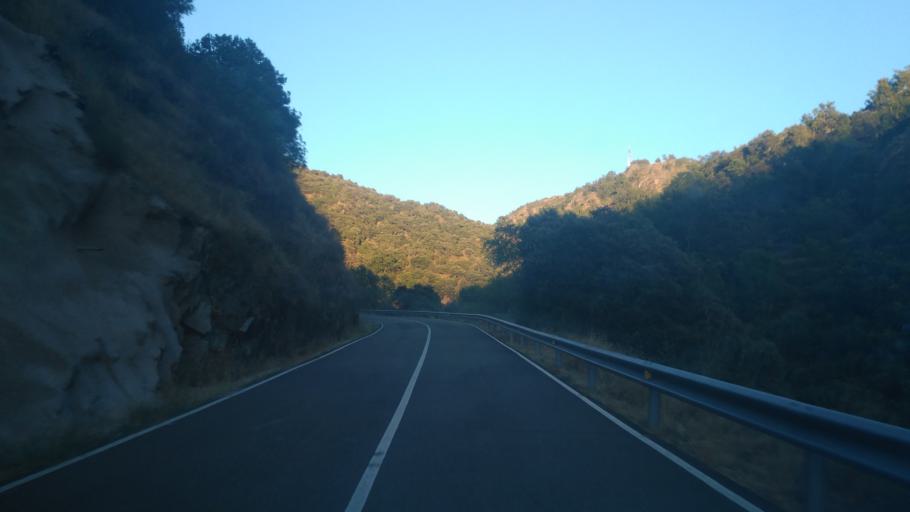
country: ES
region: Castille and Leon
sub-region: Provincia de Salamanca
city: Mieza
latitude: 41.1869
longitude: -6.6777
